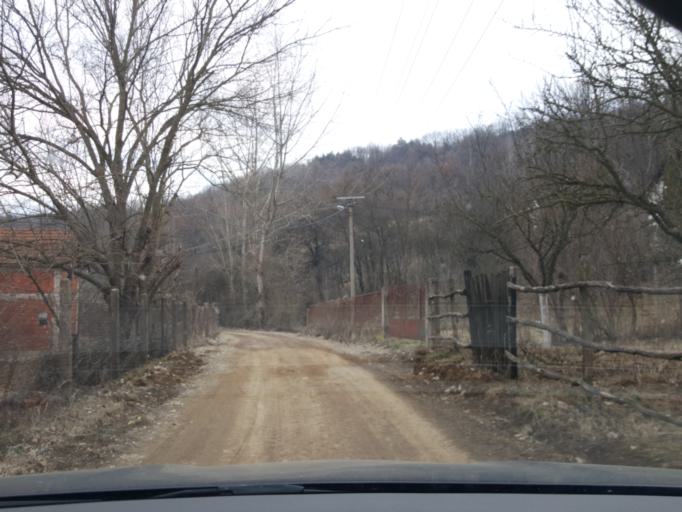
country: RS
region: Central Serbia
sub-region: Pirotski Okrug
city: Dimitrovgrad
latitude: 43.0044
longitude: 22.7580
